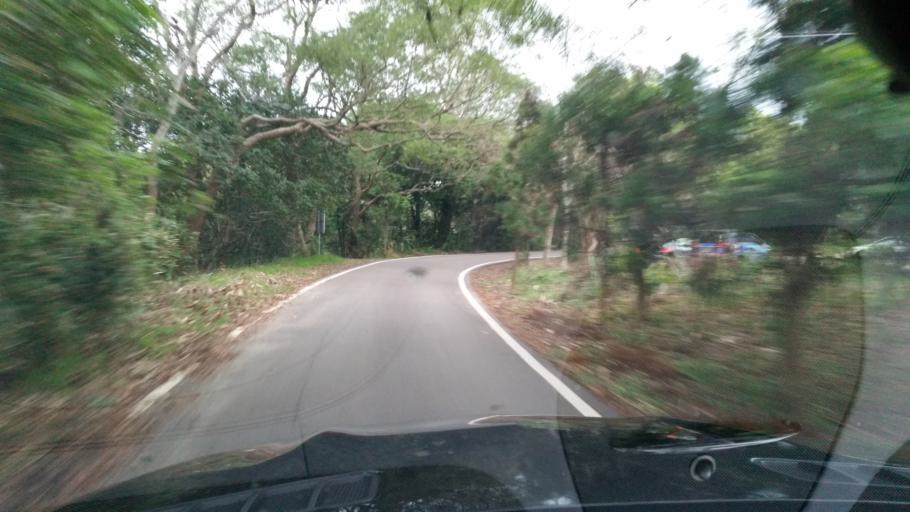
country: TW
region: Taiwan
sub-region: Miaoli
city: Miaoli
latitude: 24.5871
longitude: 120.8955
